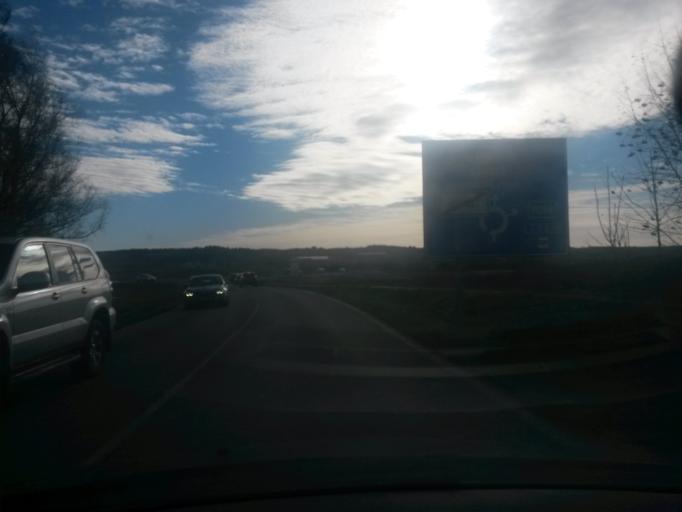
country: CZ
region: Central Bohemia
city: Jesenice
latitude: 49.9646
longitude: 14.5190
